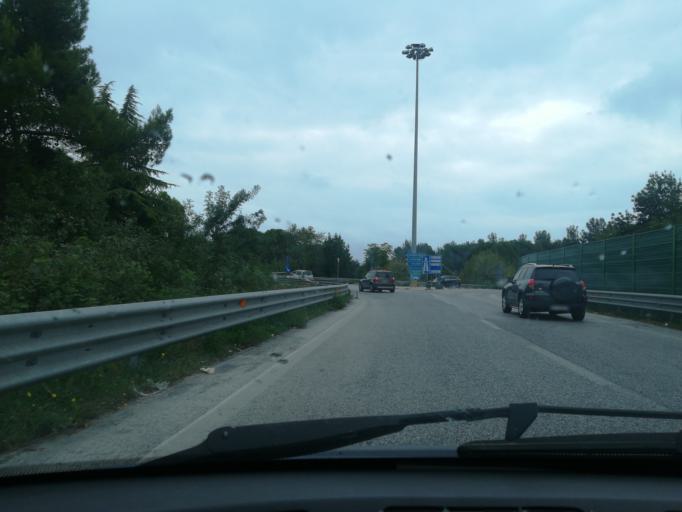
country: IT
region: The Marches
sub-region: Provincia di Macerata
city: Zona Industriale
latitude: 43.2655
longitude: 13.4898
